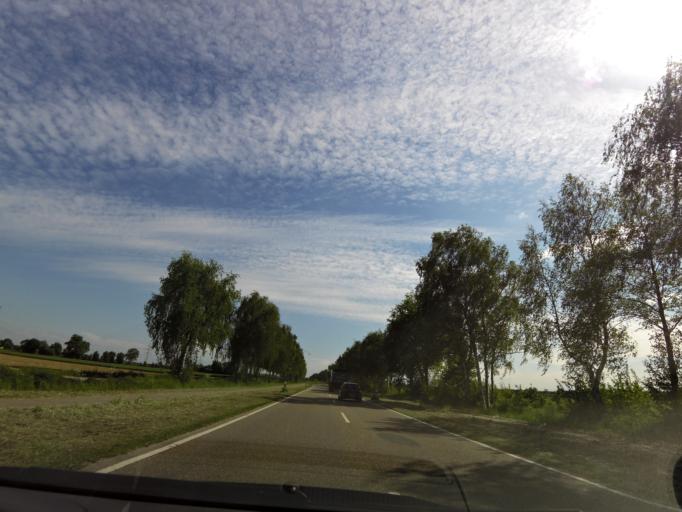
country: DE
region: North Rhine-Westphalia
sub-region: Regierungsbezirk Koln
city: Selfkant
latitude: 51.0230
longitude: 5.9443
